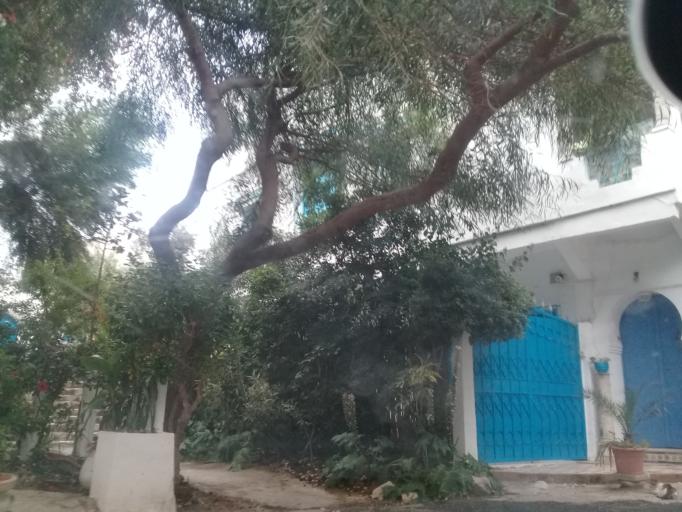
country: TN
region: Tunis
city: Sidi Bou Said
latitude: 36.8679
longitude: 10.3385
